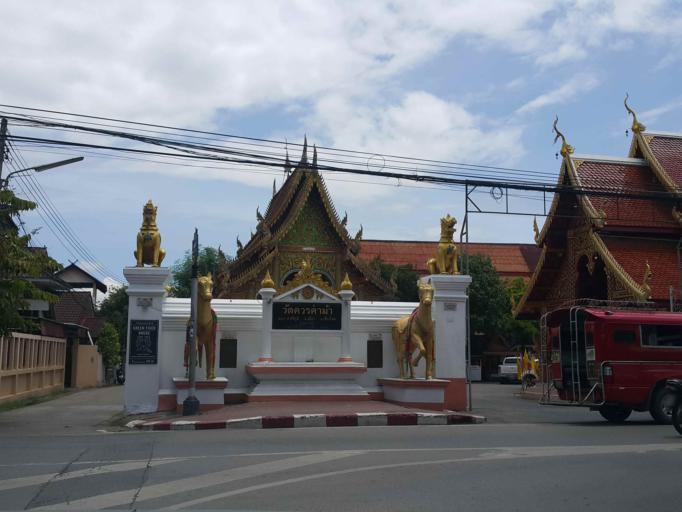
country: TH
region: Chiang Mai
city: Chiang Mai
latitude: 18.7955
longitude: 98.9841
